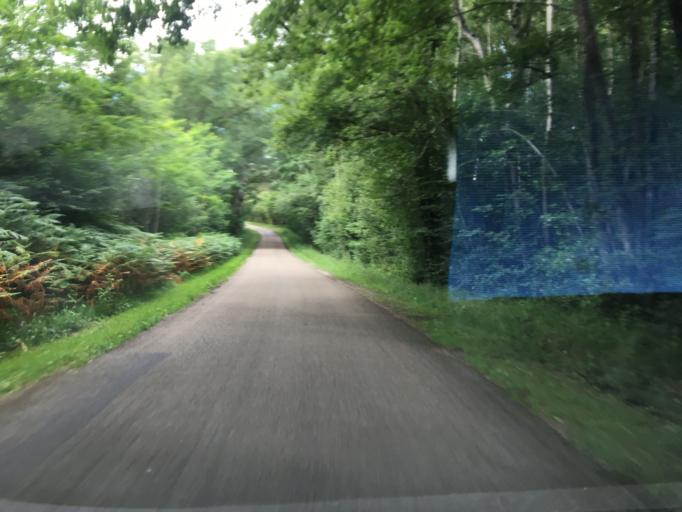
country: FR
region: Bourgogne
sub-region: Departement de l'Yonne
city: Fleury-la-Vallee
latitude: 47.8578
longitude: 3.4870
